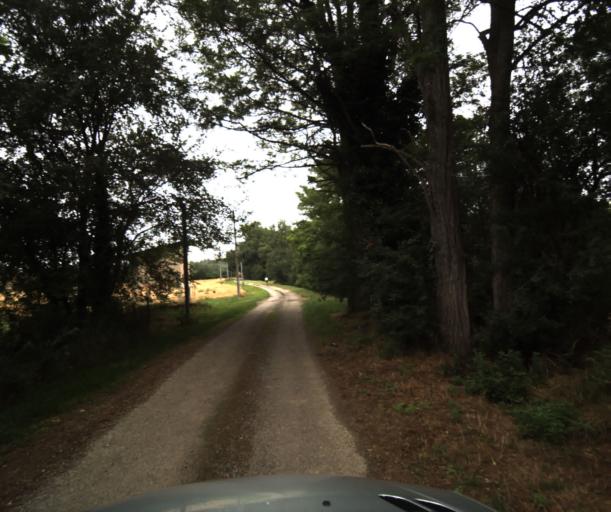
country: FR
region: Midi-Pyrenees
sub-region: Departement de la Haute-Garonne
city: Labarthe-sur-Leze
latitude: 43.4666
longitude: 1.4178
